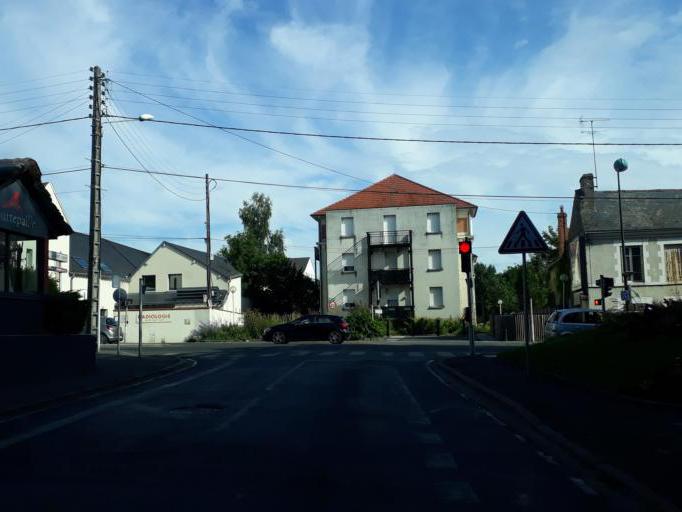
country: FR
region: Centre
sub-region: Departement du Loiret
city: Saint-Jean-le-Blanc
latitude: 47.9039
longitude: 1.9402
